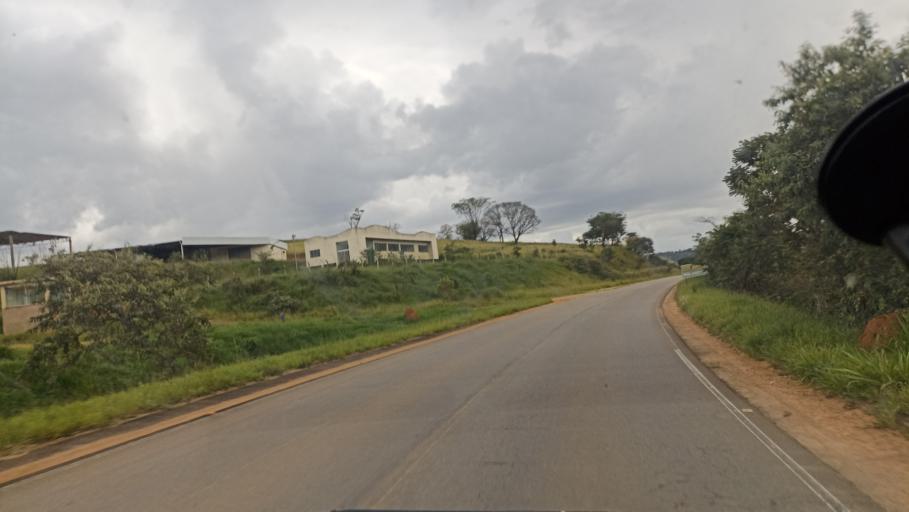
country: BR
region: Minas Gerais
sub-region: Cruzilia
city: Cruzilia
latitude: -21.8905
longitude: -44.8150
